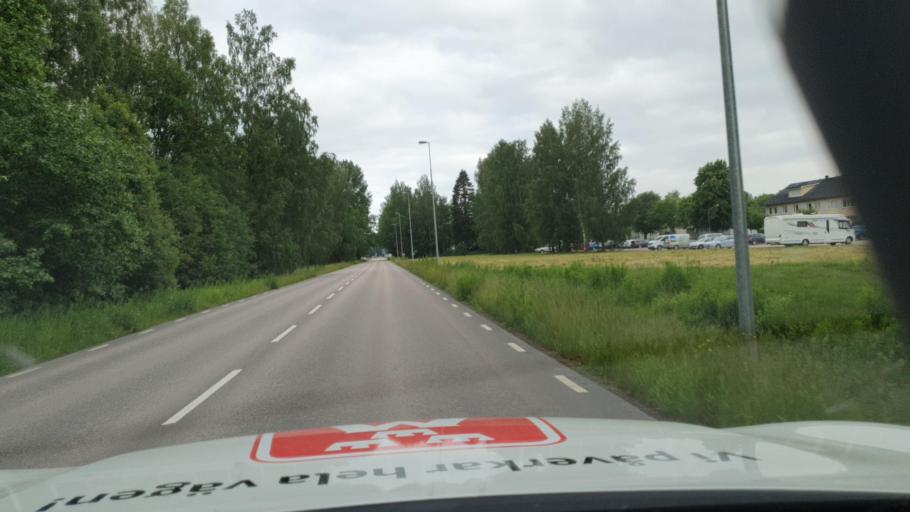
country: SE
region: Vaermland
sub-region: Karlstads Kommun
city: Karlstad
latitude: 59.4394
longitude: 13.4424
